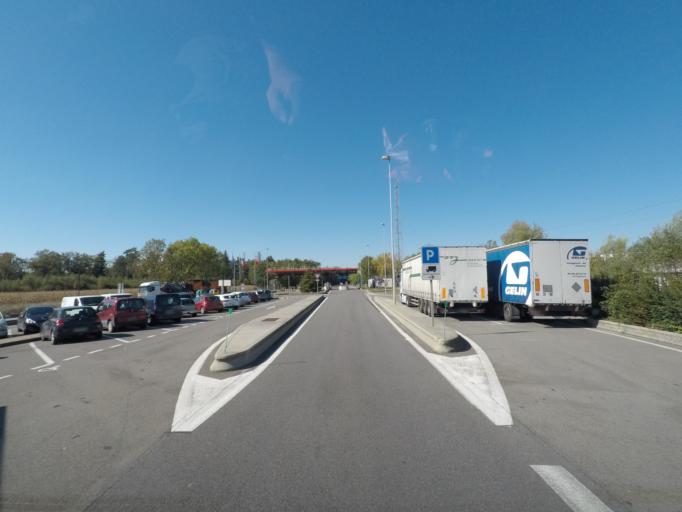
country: FR
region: Rhone-Alpes
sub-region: Departement de l'Ain
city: Attignat
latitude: 46.2599
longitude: 5.1684
